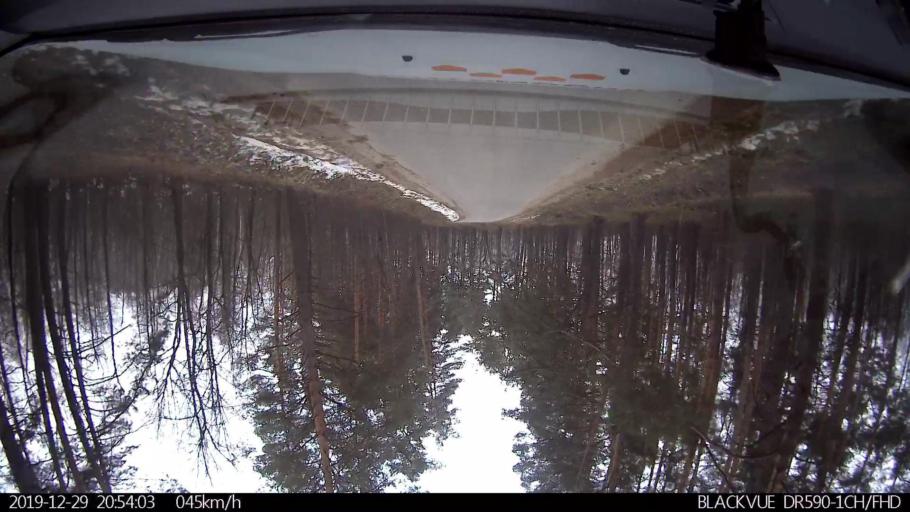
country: RU
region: Nizjnij Novgorod
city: Afonino
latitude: 56.1668
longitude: 43.9877
